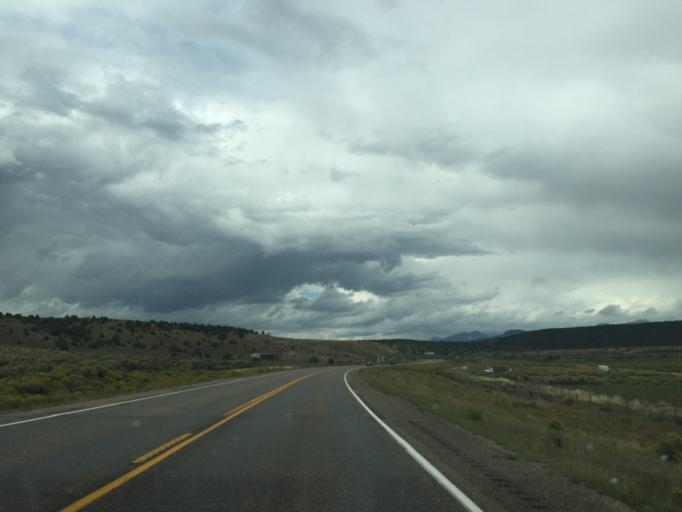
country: US
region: Utah
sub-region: Garfield County
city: Panguitch
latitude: 37.7437
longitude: -112.3796
